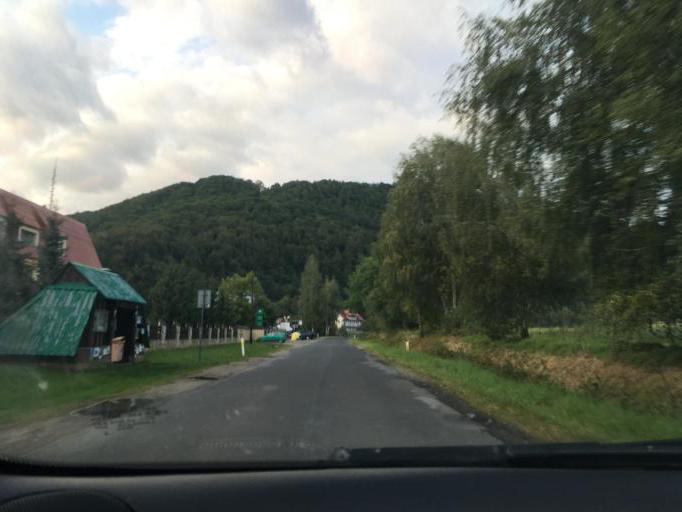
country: PL
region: Subcarpathian Voivodeship
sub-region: Powiat leski
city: Polanczyk
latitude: 49.3067
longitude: 22.4177
